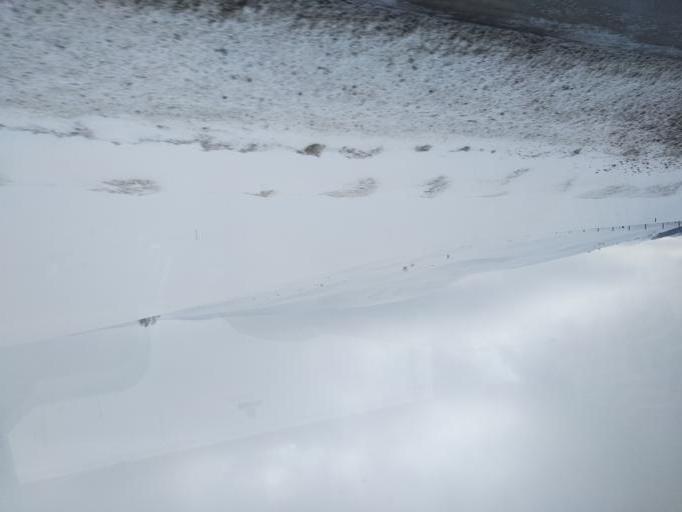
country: TR
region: Erzincan
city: Catalarmut
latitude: 39.8907
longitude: 39.3624
